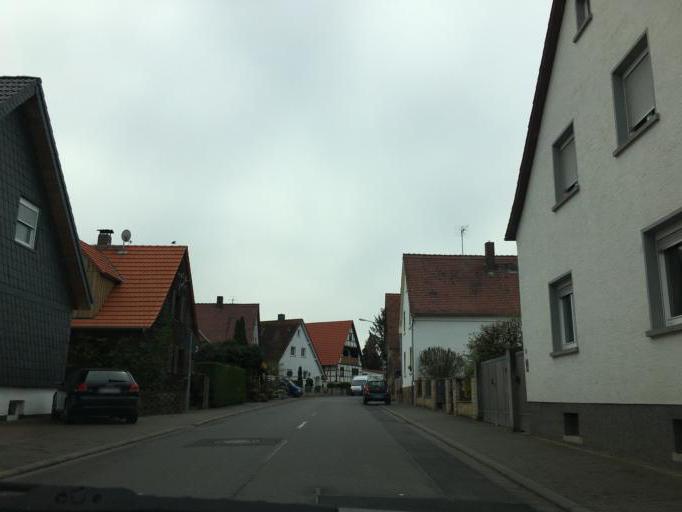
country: DE
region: Hesse
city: Reinheim
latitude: 49.8477
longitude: 8.8790
